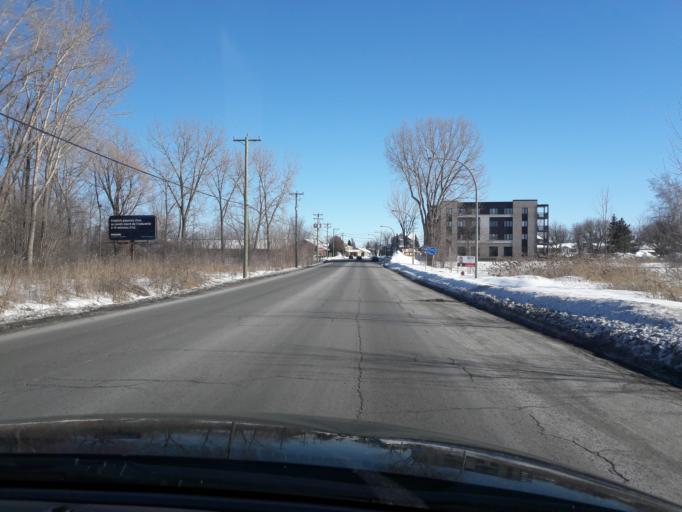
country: CA
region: Quebec
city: Dollard-Des Ormeaux
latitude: 45.5429
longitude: -73.7905
